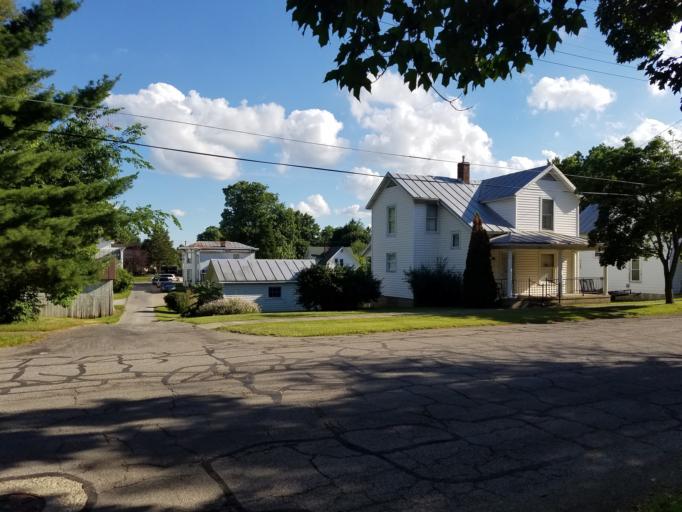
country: US
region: Ohio
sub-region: Morrow County
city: Mount Gilead
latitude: 40.5504
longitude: -82.8387
